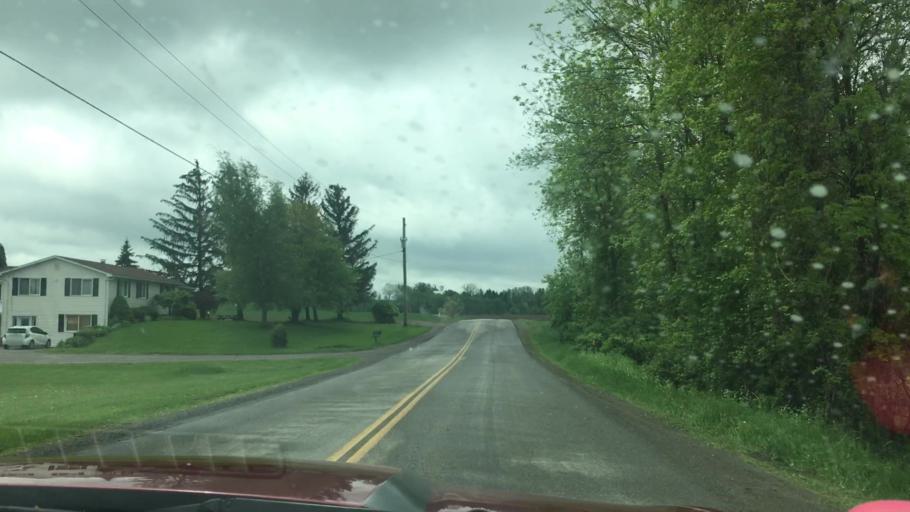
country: US
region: New York
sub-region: Genesee County
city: Batavia
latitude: 43.0921
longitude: -78.1385
